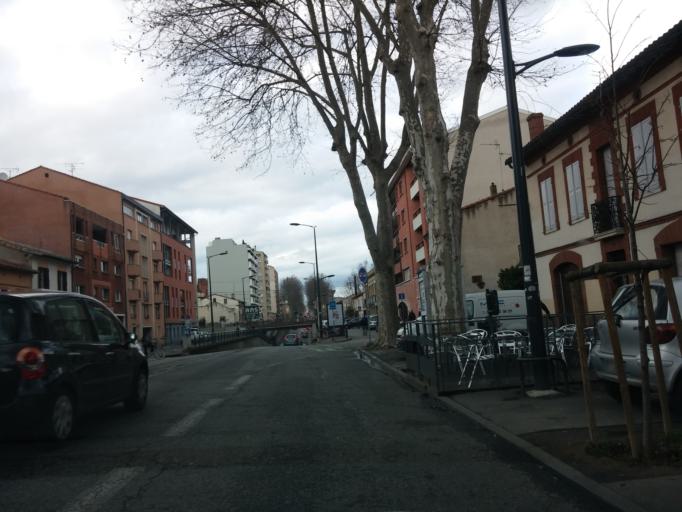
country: FR
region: Midi-Pyrenees
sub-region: Departement de la Haute-Garonne
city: Toulouse
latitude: 43.5782
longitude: 1.4504
